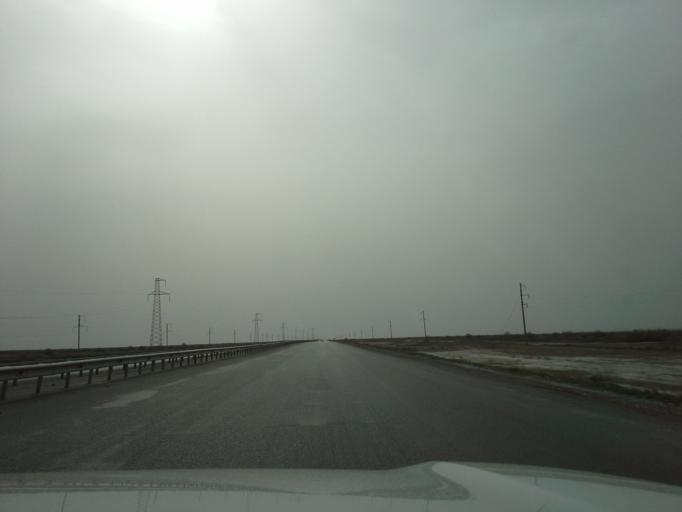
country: TM
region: Ahal
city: Kaka
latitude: 37.5378
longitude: 59.4039
